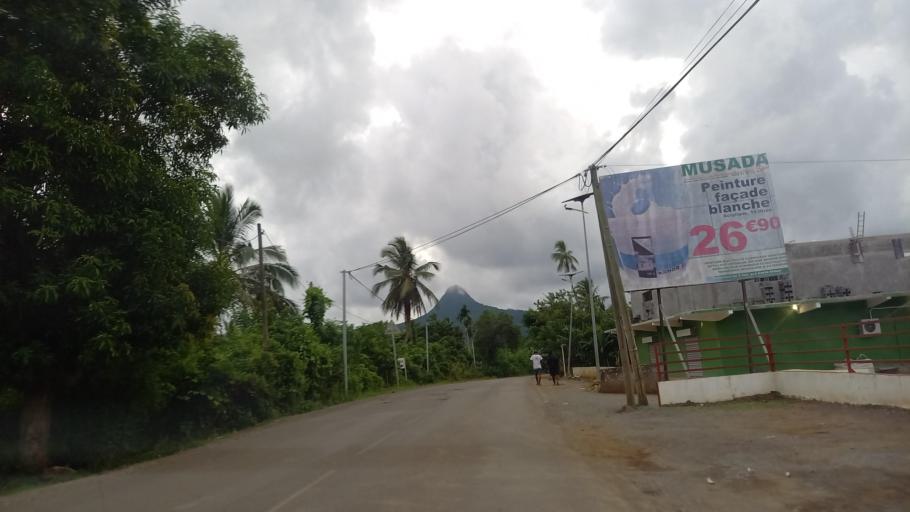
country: YT
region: Chirongui
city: Chirongui
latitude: -12.9231
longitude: 45.1571
